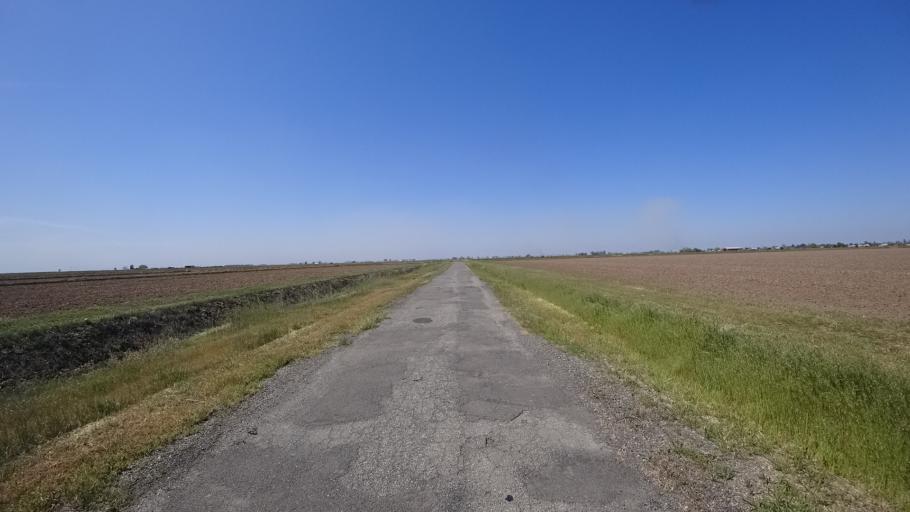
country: US
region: California
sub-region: Glenn County
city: Willows
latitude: 39.5653
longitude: -122.0243
